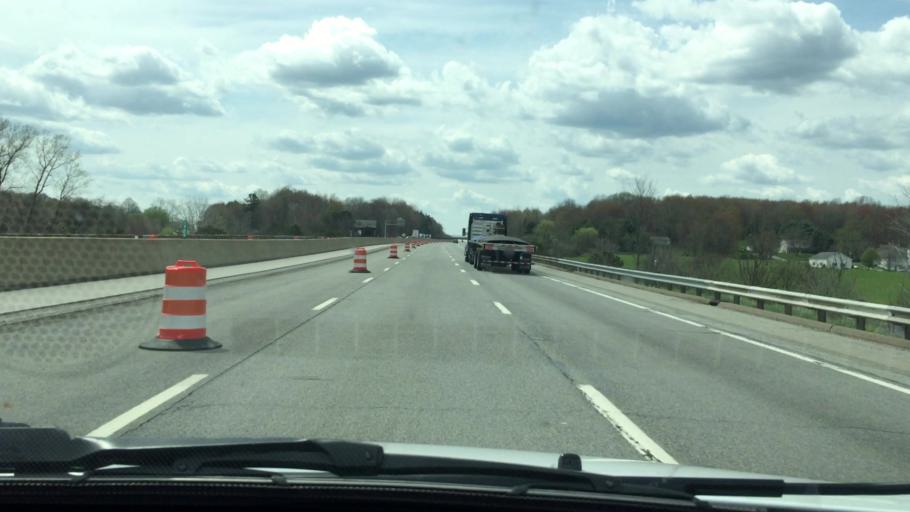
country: US
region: Ohio
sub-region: Portage County
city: Mantua
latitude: 41.2462
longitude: -81.2551
